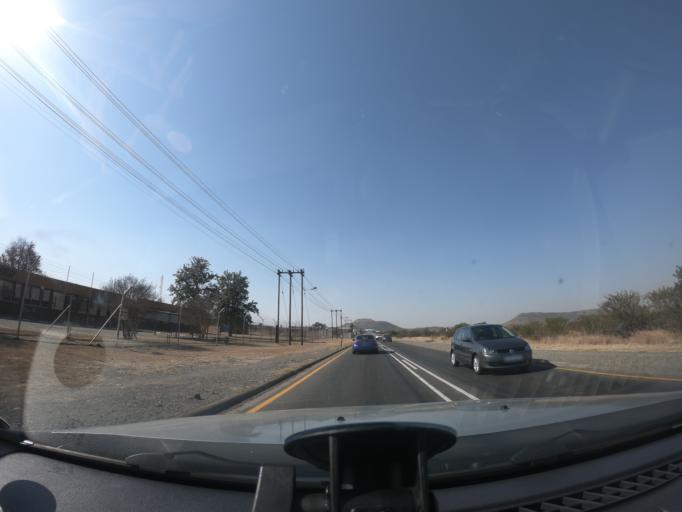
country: ZA
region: KwaZulu-Natal
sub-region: uThukela District Municipality
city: Ladysmith
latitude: -28.5445
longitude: 29.8128
